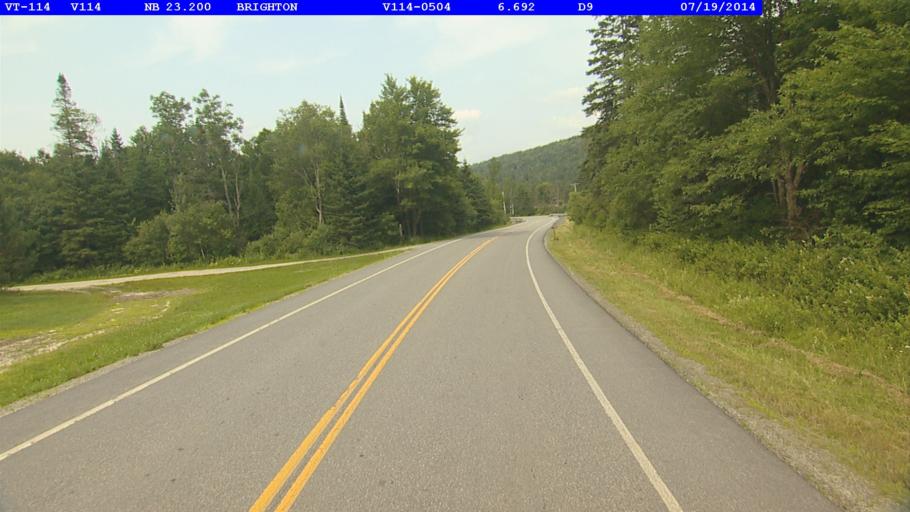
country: US
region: Vermont
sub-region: Orleans County
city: Newport
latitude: 44.8375
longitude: -71.9081
